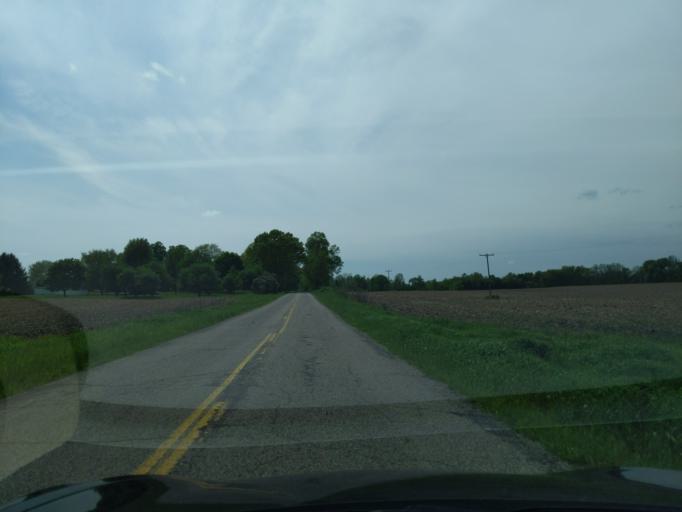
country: US
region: Michigan
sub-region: Ingham County
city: Leslie
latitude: 42.4319
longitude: -84.3395
